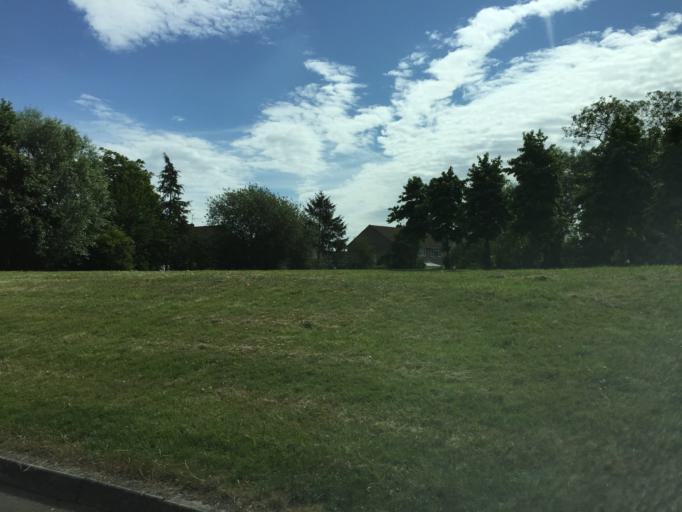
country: GB
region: Wales
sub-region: Newport
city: Nash
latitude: 51.5727
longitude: -2.9590
